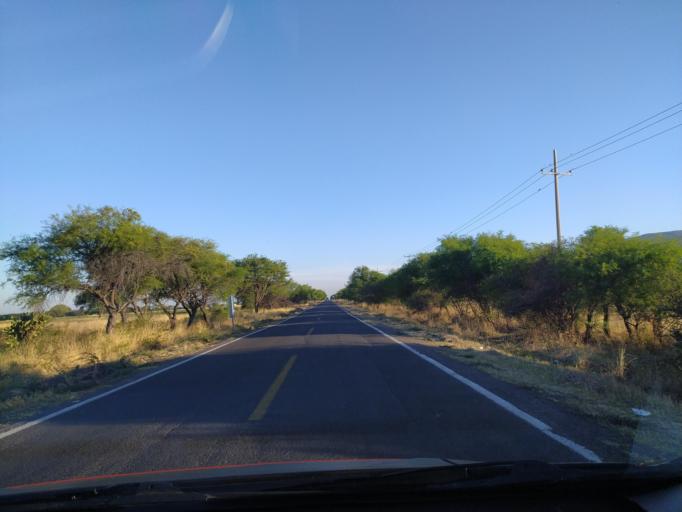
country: MX
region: Guanajuato
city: Ciudad Manuel Doblado
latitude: 20.7564
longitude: -101.8266
